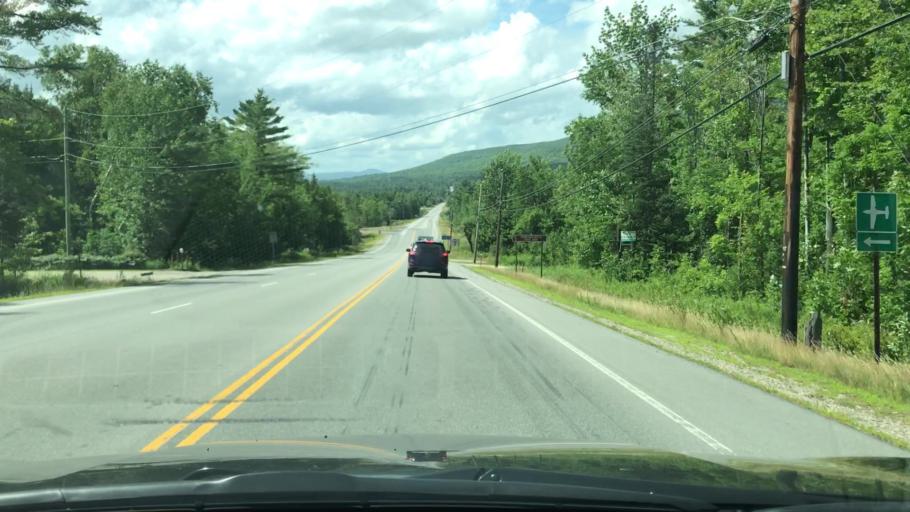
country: US
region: New Hampshire
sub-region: Coos County
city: Jefferson
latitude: 44.3787
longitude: -71.4146
